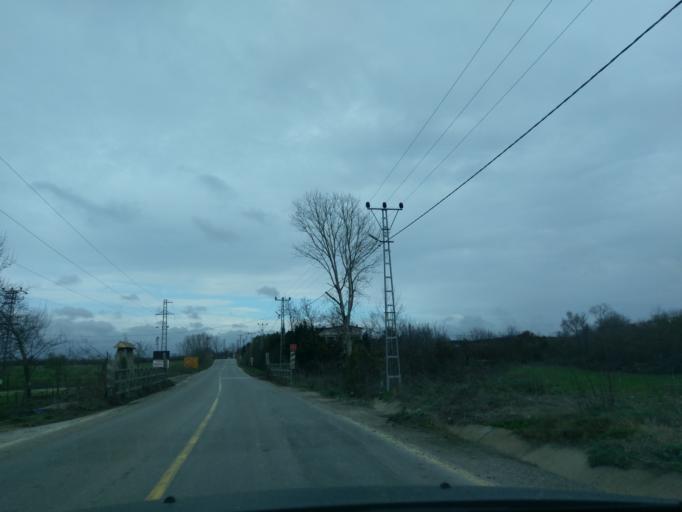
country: TR
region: Istanbul
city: Catalca
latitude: 41.2024
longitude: 28.3871
